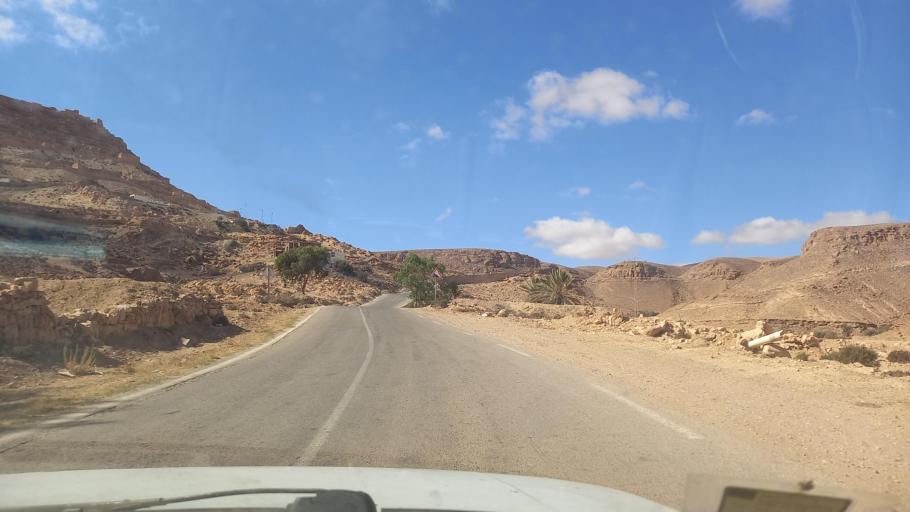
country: TN
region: Tataouine
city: Tataouine
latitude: 32.9161
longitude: 10.2637
